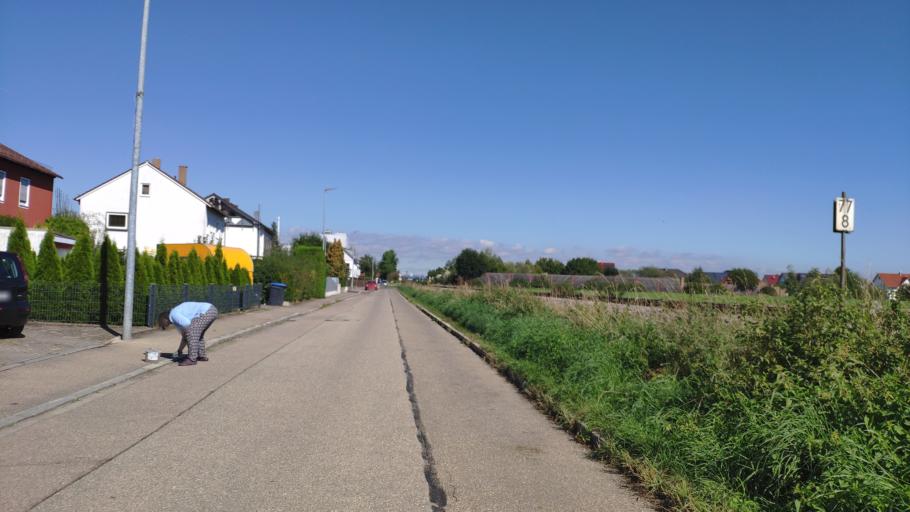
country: DE
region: Bavaria
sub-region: Swabia
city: Senden
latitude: 48.3473
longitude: 10.0383
